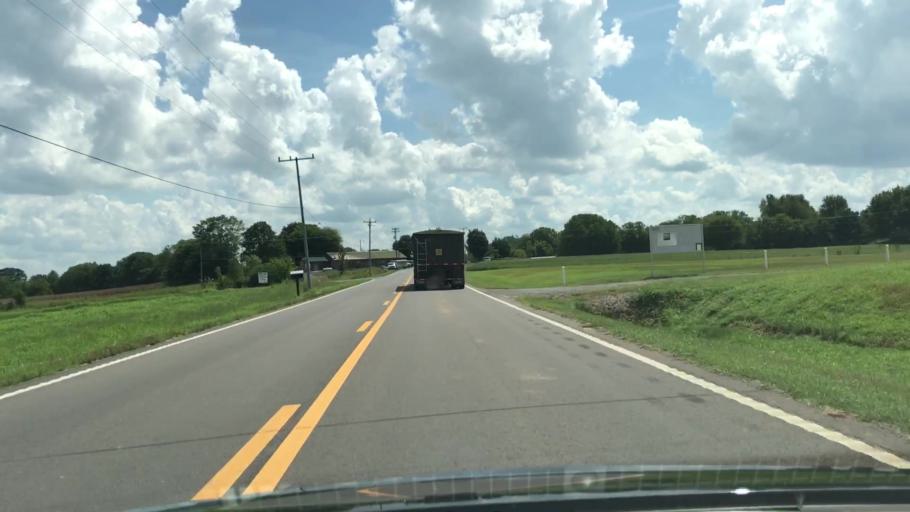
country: US
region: Tennessee
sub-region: Robertson County
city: Springfield
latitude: 36.6029
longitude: -86.9213
